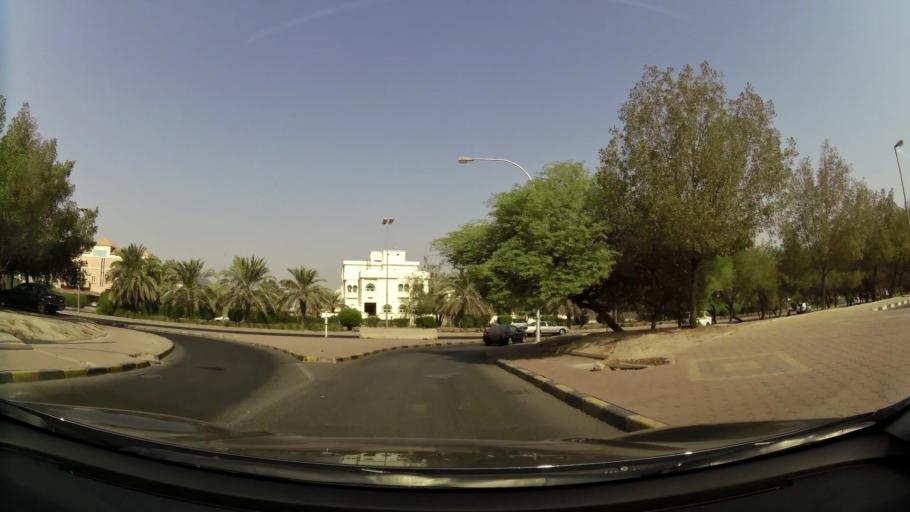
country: KW
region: Al Asimah
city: Ad Dasmah
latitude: 29.3443
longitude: 48.0074
